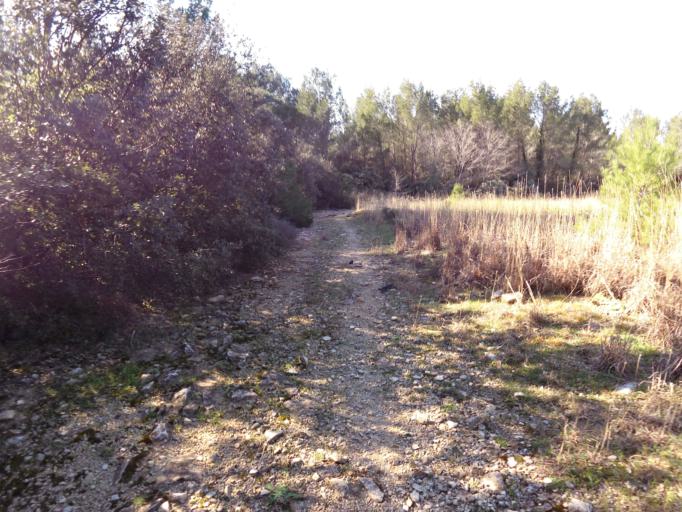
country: FR
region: Languedoc-Roussillon
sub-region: Departement du Gard
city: Congenies
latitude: 43.7589
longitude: 4.1696
